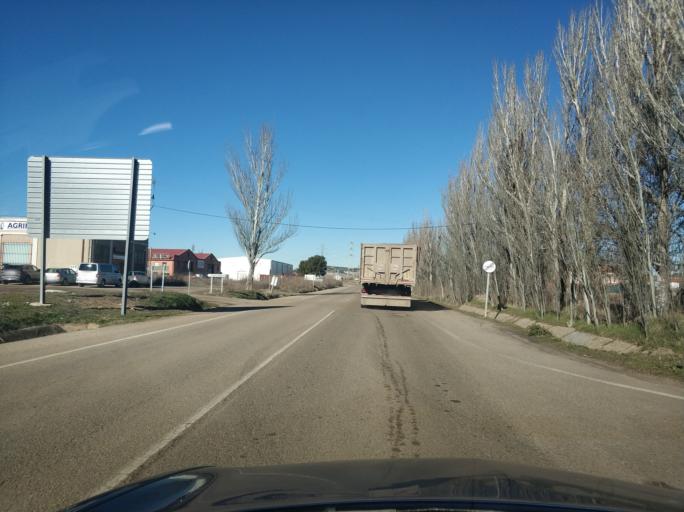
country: ES
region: Castille and Leon
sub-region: Provincia de Valladolid
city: Tordesillas
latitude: 41.5043
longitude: -5.0072
